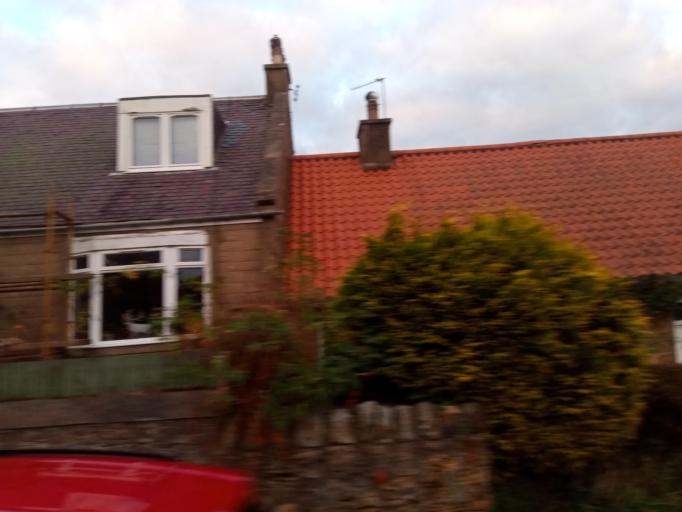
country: GB
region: Scotland
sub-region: Fife
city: Pathhead
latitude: 55.8756
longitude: -3.0034
